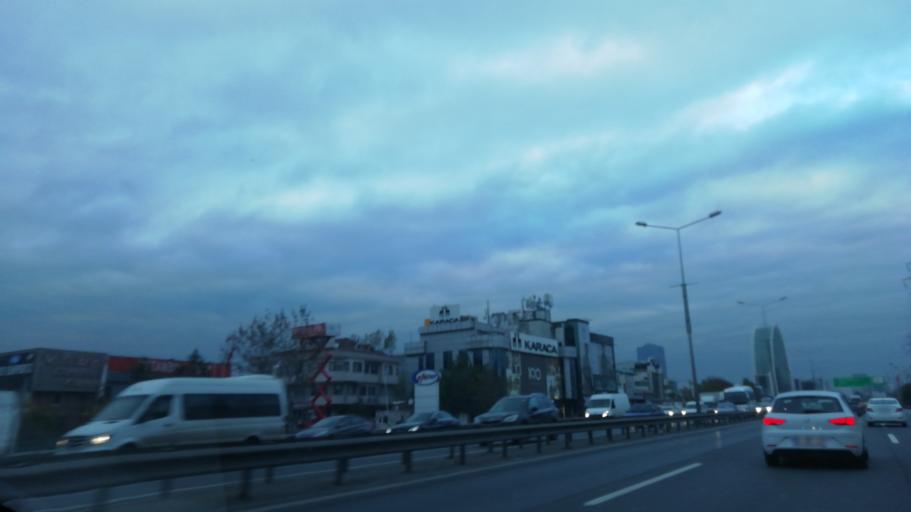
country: TR
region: Istanbul
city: Mahmutbey
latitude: 41.0209
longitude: 28.8119
